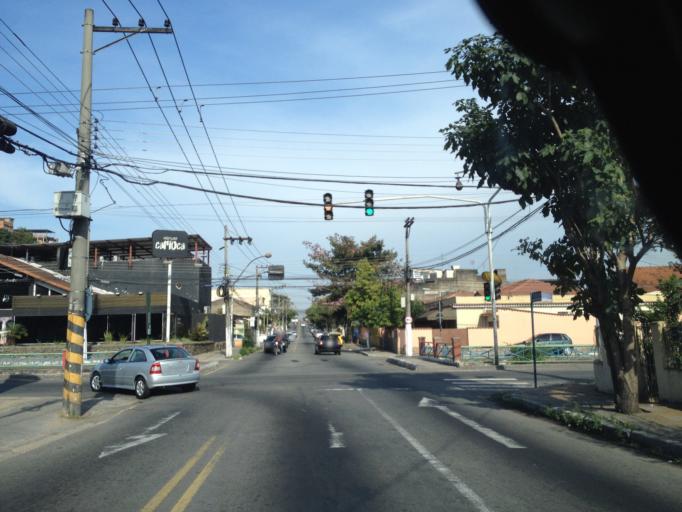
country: BR
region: Rio de Janeiro
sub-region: Volta Redonda
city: Volta Redonda
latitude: -22.5211
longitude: -44.1164
